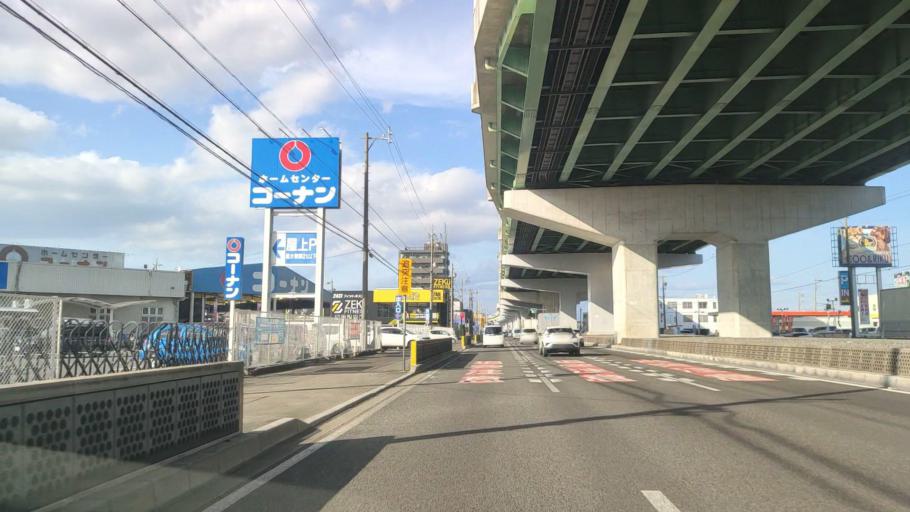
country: JP
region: Aichi
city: Ichinomiya
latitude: 35.2800
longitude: 136.8298
